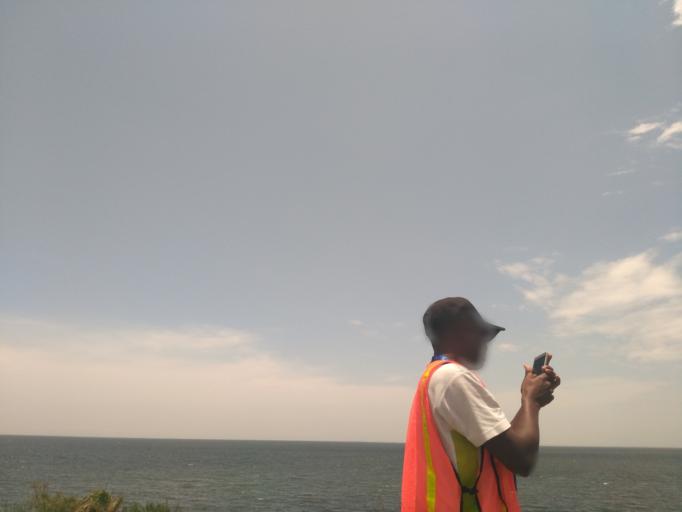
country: TZ
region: Mwanza
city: Mwanza
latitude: -2.4435
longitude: 32.9080
